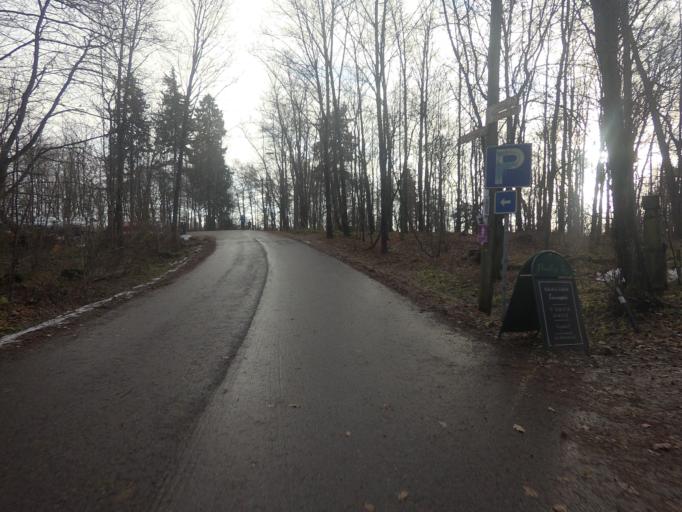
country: FI
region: Uusimaa
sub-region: Helsinki
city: Teekkarikylae
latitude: 60.2064
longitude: 24.8399
